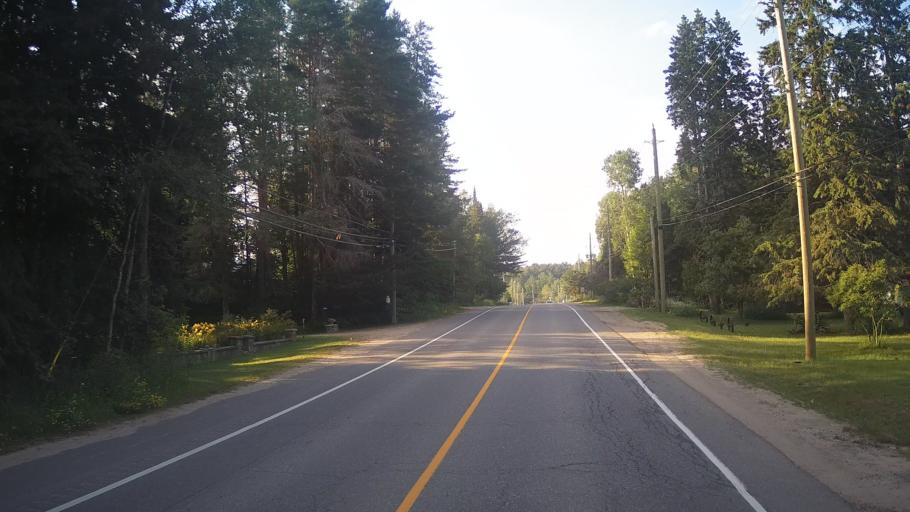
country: CA
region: Ontario
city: Huntsville
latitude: 45.3480
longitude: -79.2014
